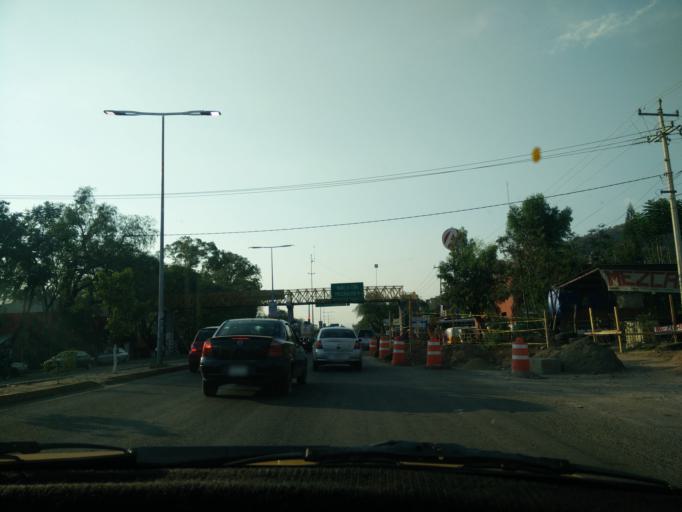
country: MX
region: Oaxaca
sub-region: Santa Maria Atzompa
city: San Jeronimo Yahuiche
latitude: 17.1007
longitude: -96.7513
